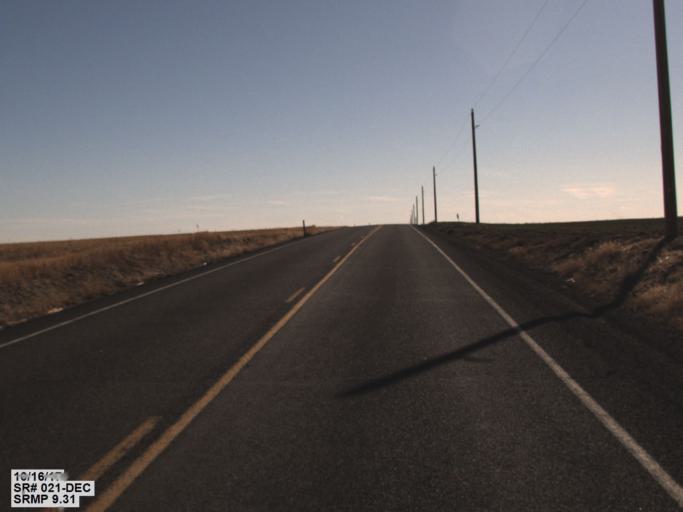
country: US
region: Washington
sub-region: Franklin County
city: Connell
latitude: 46.7610
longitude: -118.5476
